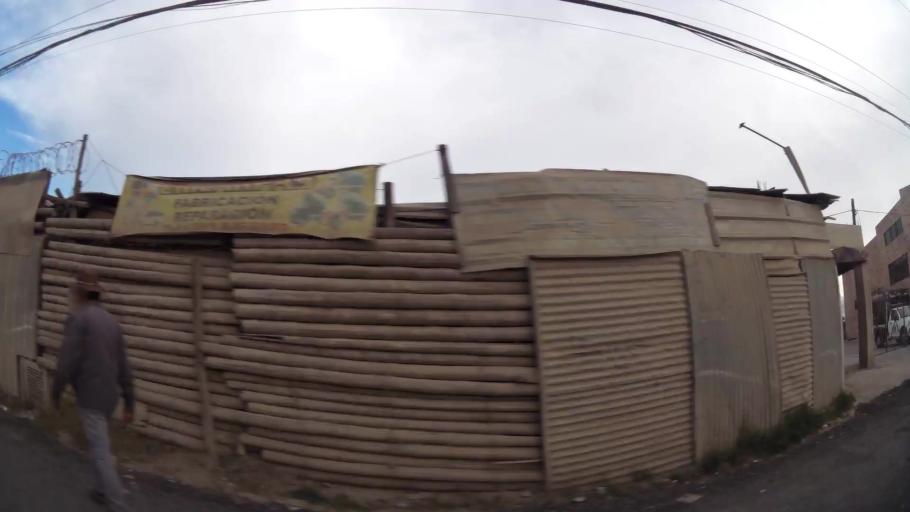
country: CO
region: Cundinamarca
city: Funza
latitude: 4.6954
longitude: -74.1747
